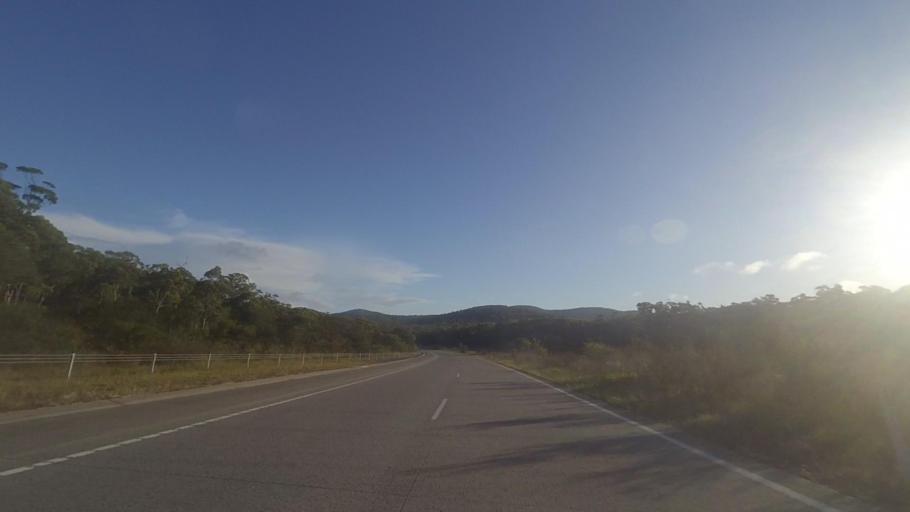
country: AU
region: New South Wales
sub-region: Great Lakes
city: Bulahdelah
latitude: -32.4793
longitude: 152.1932
